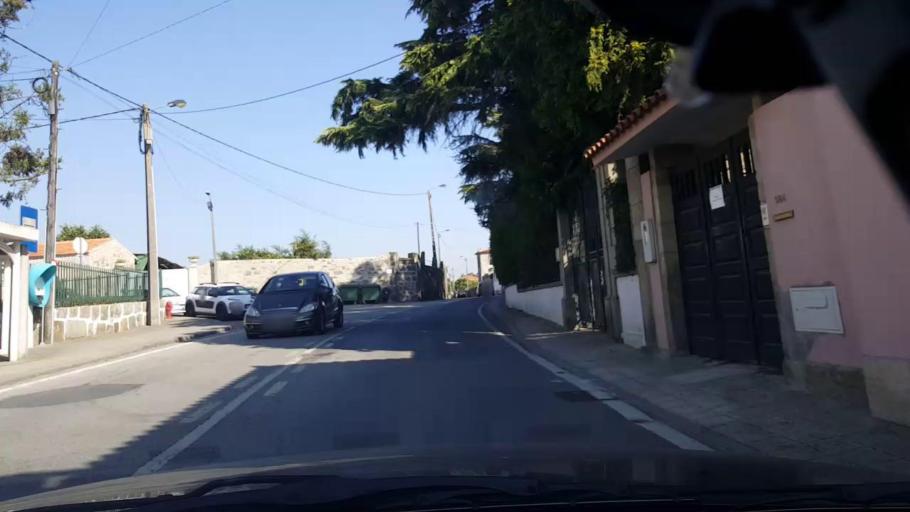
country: PT
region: Porto
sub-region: Vila do Conde
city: Arvore
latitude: 41.3076
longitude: -8.6791
